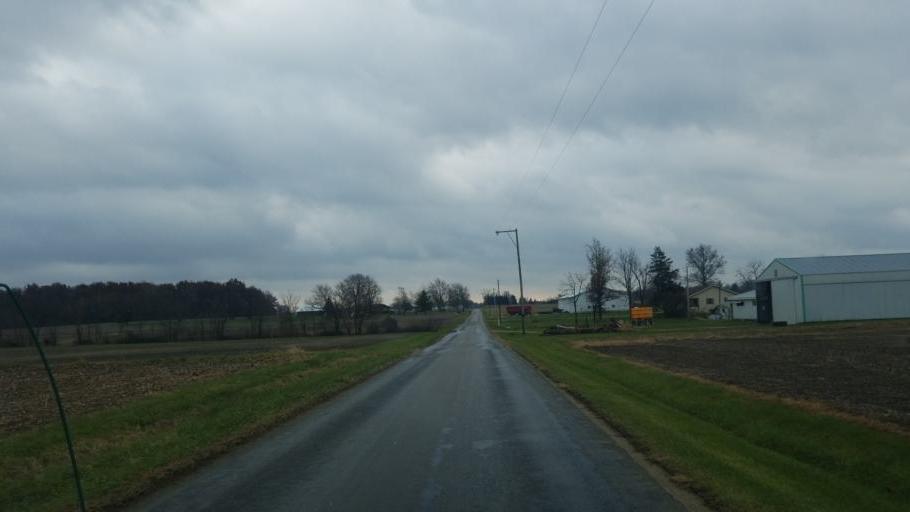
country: US
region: Indiana
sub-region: Adams County
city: Geneva
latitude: 40.5464
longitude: -84.9916
